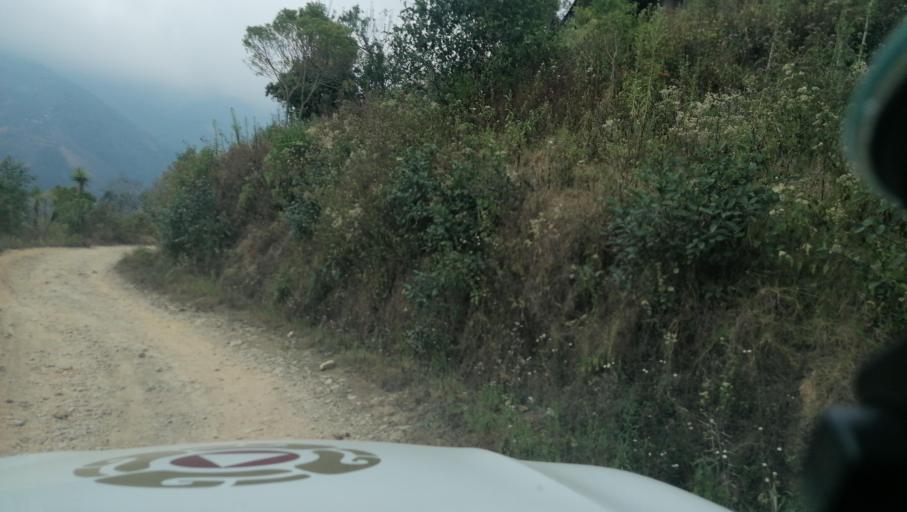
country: GT
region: San Marcos
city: Tacana
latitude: 15.2183
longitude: -92.1969
